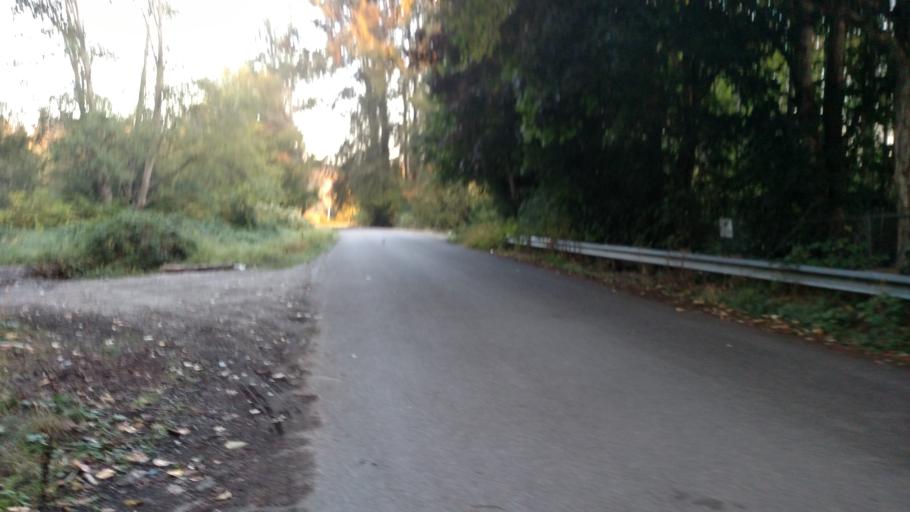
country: US
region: Washington
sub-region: King County
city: Kent
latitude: 47.3872
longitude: -122.2708
